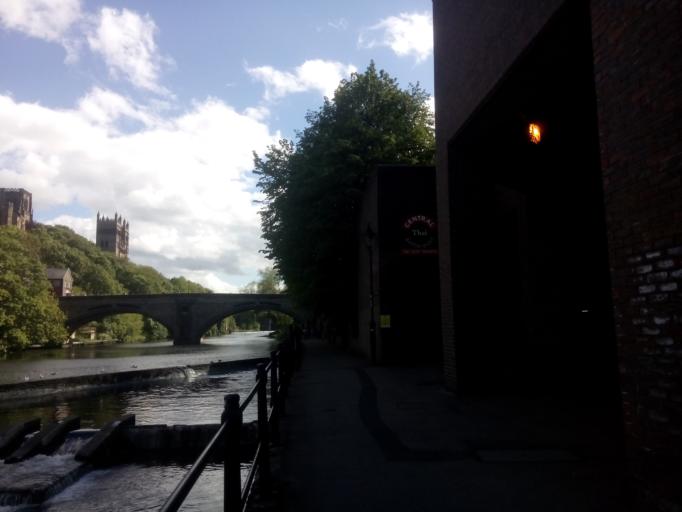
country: GB
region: England
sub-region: County Durham
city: Durham
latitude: 54.7773
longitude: -1.5781
